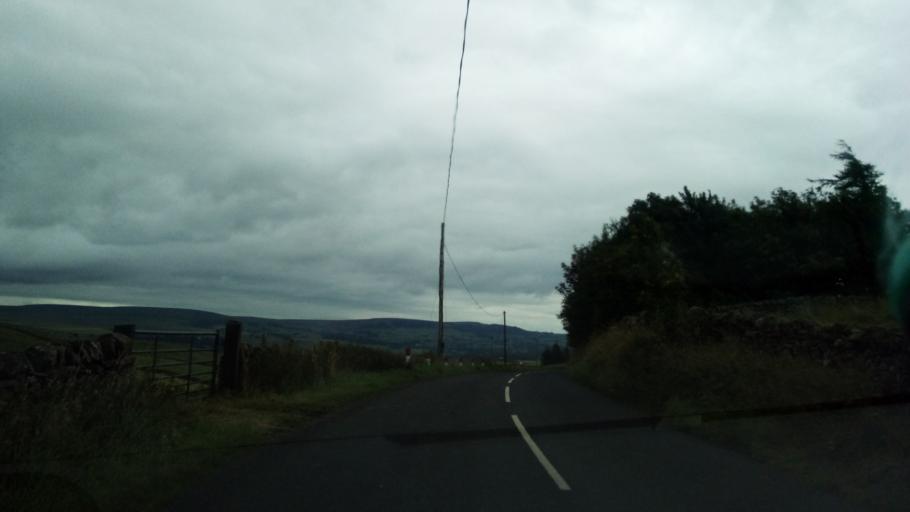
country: GB
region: England
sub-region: County Durham
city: Mickleton
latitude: 54.6067
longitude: -2.0975
